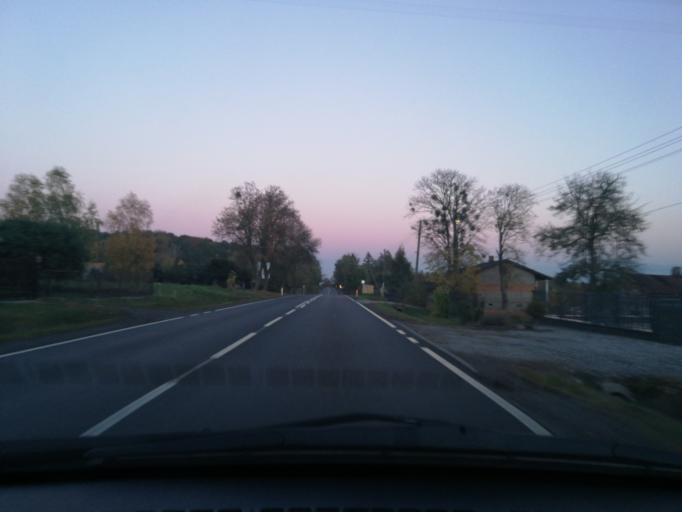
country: PL
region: Lodz Voivodeship
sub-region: Powiat brzezinski
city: Brzeziny
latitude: 51.8045
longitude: 19.6916
